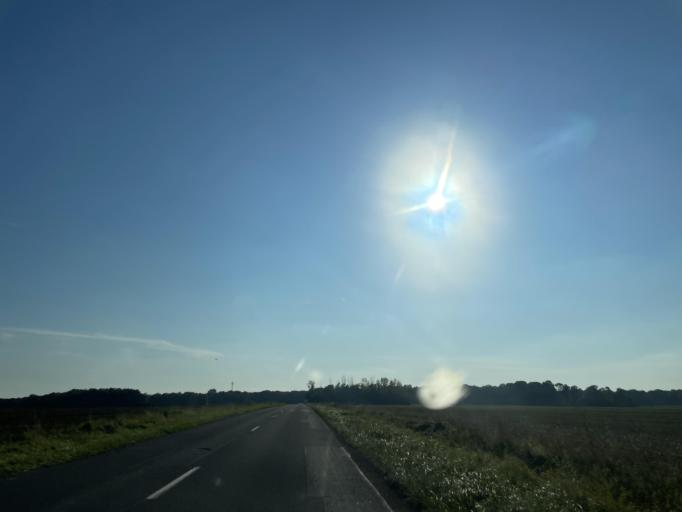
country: FR
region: Ile-de-France
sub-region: Departement de Seine-et-Marne
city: Voulangis
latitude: 48.8381
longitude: 2.8856
